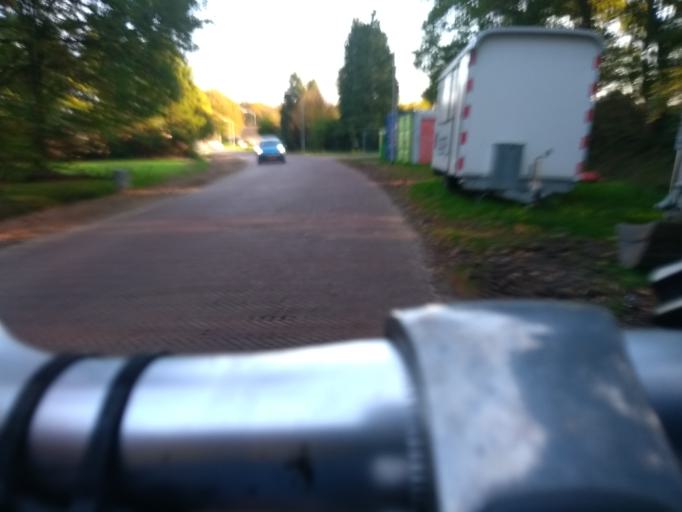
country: NL
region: Drenthe
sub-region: Gemeente Assen
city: Assen
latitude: 52.9794
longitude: 6.5185
